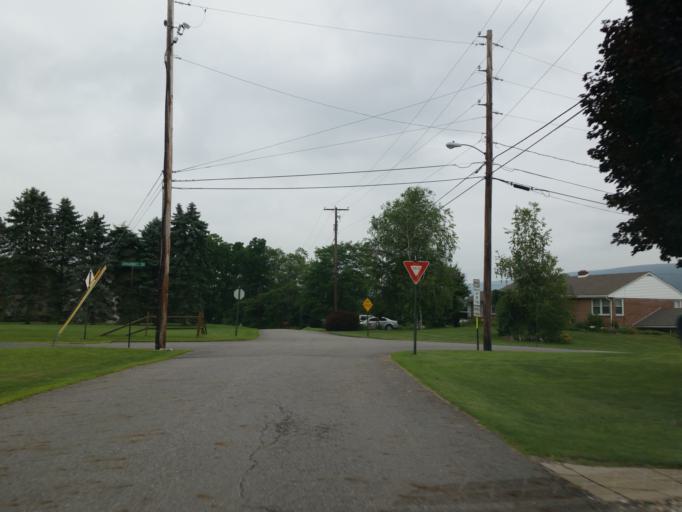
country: US
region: Pennsylvania
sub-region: Schuylkill County
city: Tower City
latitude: 40.5778
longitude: -76.5322
